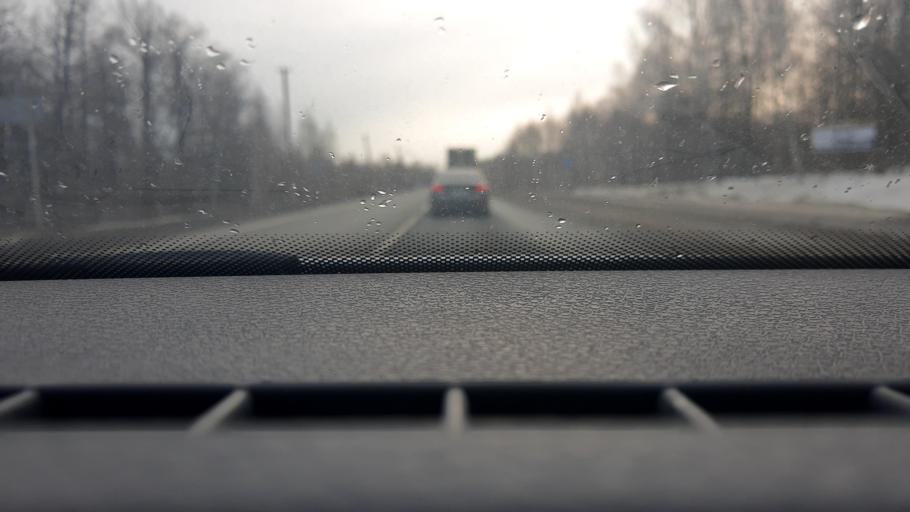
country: RU
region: Bashkortostan
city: Ulu-Telyak
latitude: 54.8414
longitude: 57.0557
